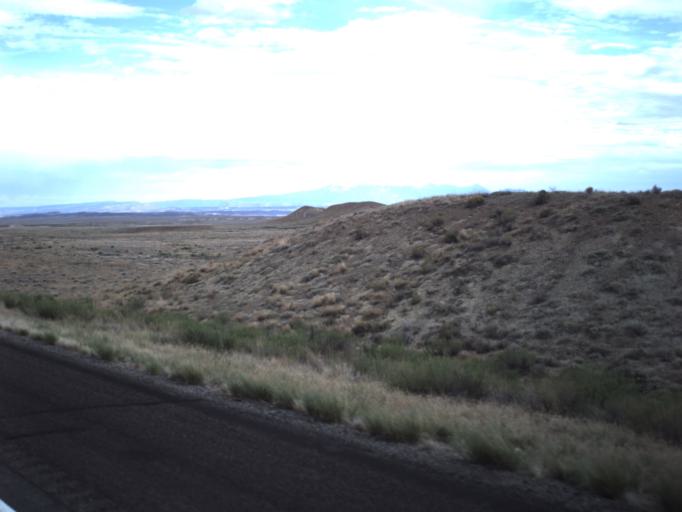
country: US
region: Utah
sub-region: Grand County
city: Moab
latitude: 38.9477
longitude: -109.6657
